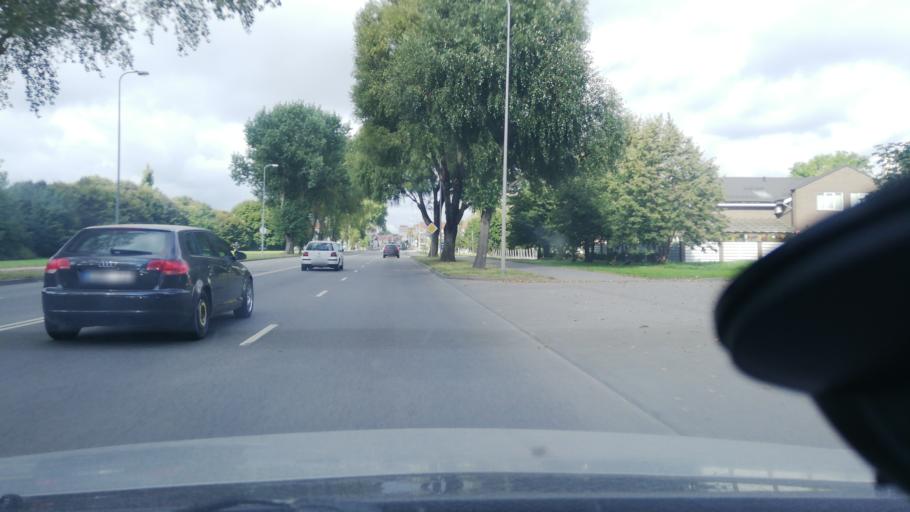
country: LT
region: Klaipedos apskritis
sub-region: Klaipeda
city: Klaipeda
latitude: 55.6727
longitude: 21.1571
